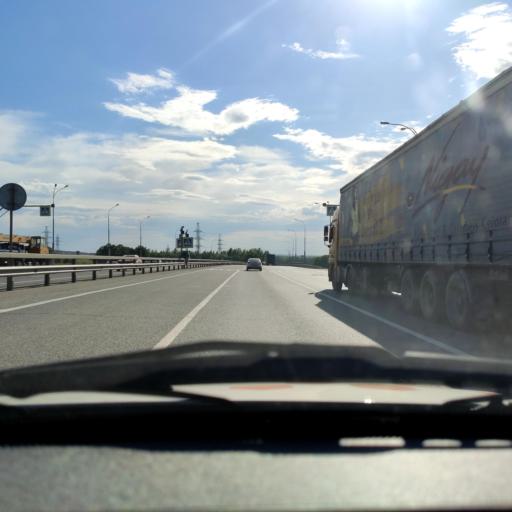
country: RU
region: Bashkortostan
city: Kabakovo
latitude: 54.6542
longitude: 56.1151
